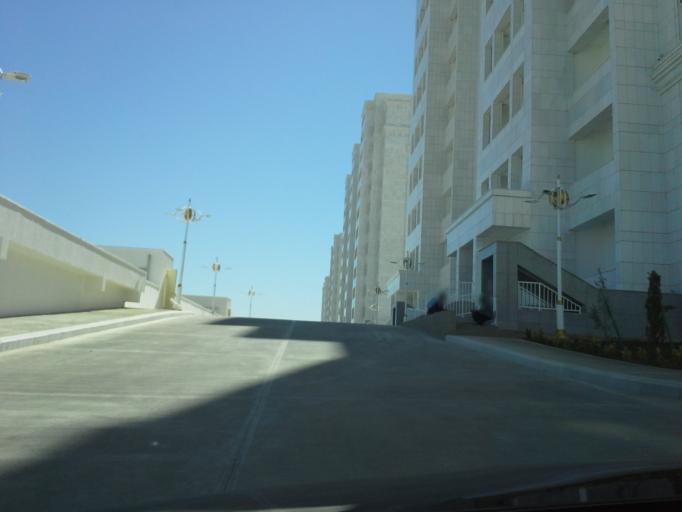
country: TM
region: Ahal
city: Ashgabat
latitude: 37.9424
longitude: 58.3500
